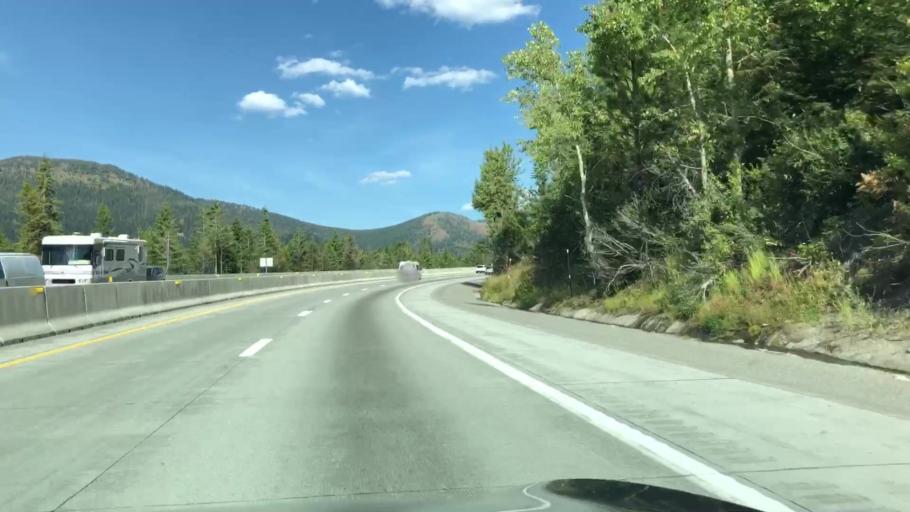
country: US
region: Idaho
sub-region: Shoshone County
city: Wallace
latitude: 47.4605
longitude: -115.7166
